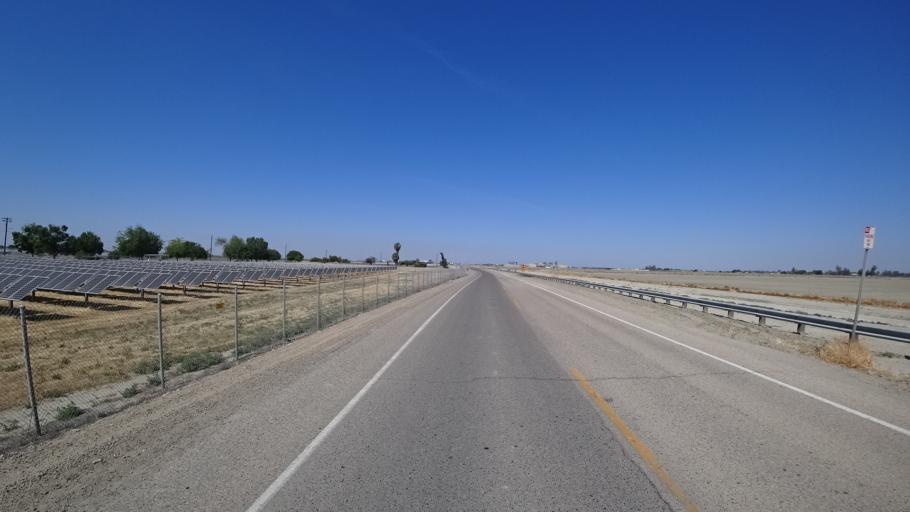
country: US
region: California
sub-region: Kings County
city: Corcoran
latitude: 36.0651
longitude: -119.5548
